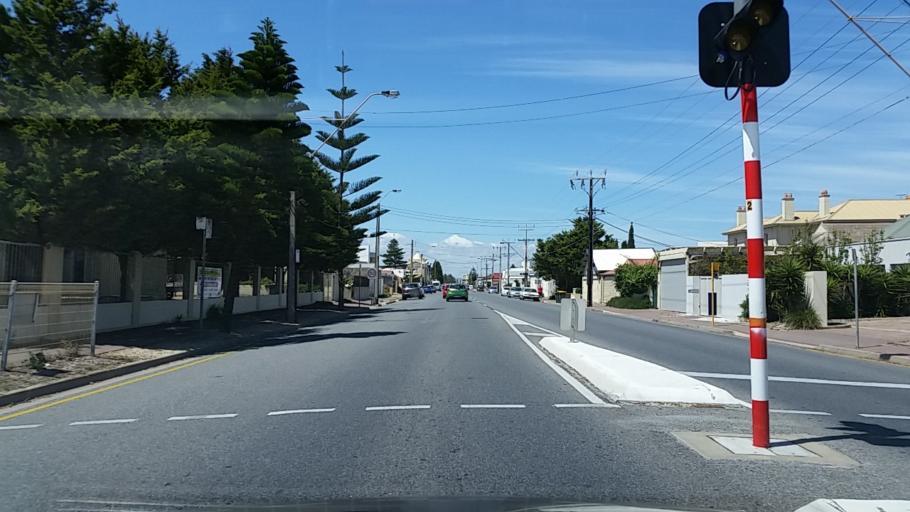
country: AU
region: South Australia
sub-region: Charles Sturt
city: Henley Beach
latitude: -34.9145
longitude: 138.4930
